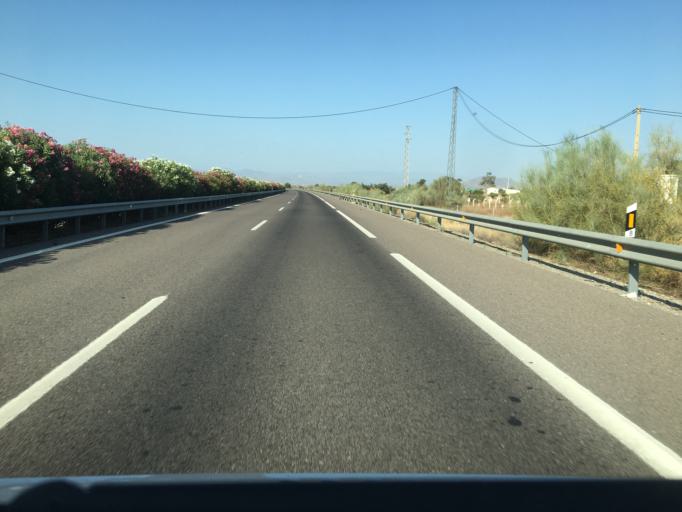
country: ES
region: Andalusia
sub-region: Provincia de Almeria
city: Huercal-Overa
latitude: 37.4340
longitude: -1.9145
